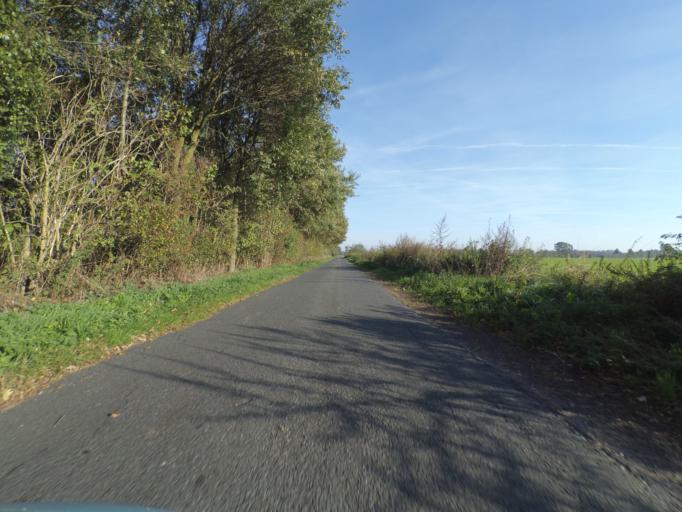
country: NL
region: Gelderland
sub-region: Berkelland
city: Eibergen
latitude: 52.0658
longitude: 6.7243
